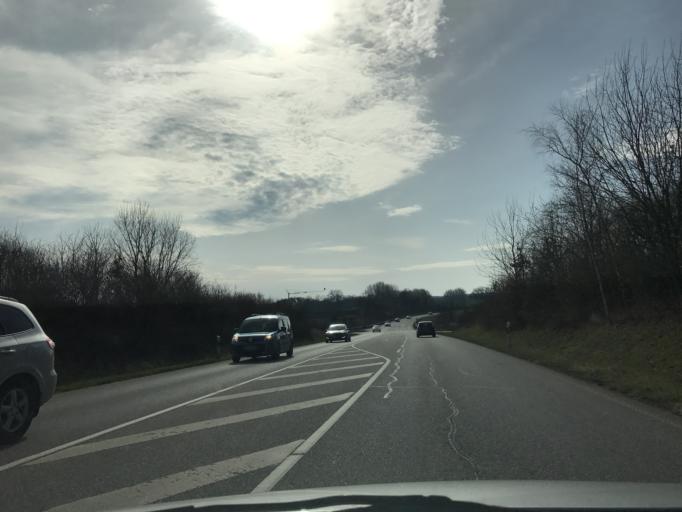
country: DE
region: Schleswig-Holstein
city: Klein Wittensee
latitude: 54.3925
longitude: 9.7299
